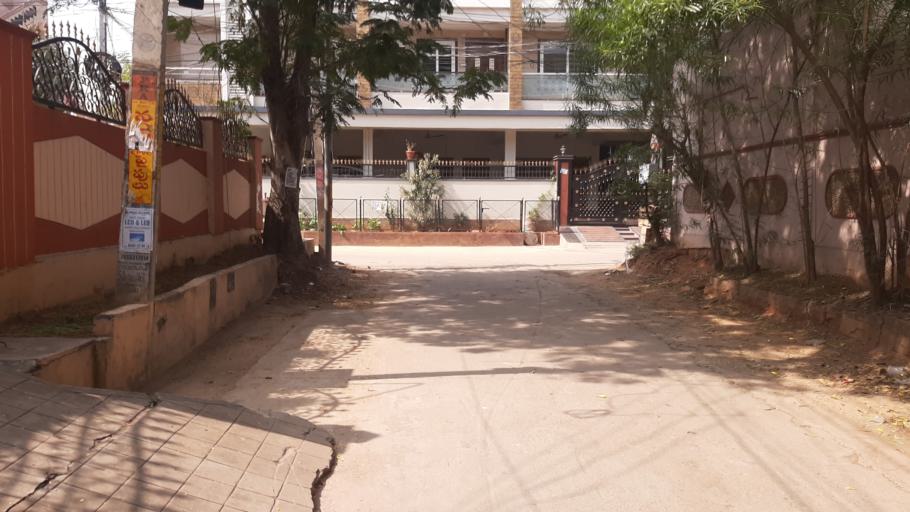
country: IN
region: Telangana
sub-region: Rangareddi
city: Lal Bahadur Nagar
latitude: 17.3465
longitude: 78.5555
